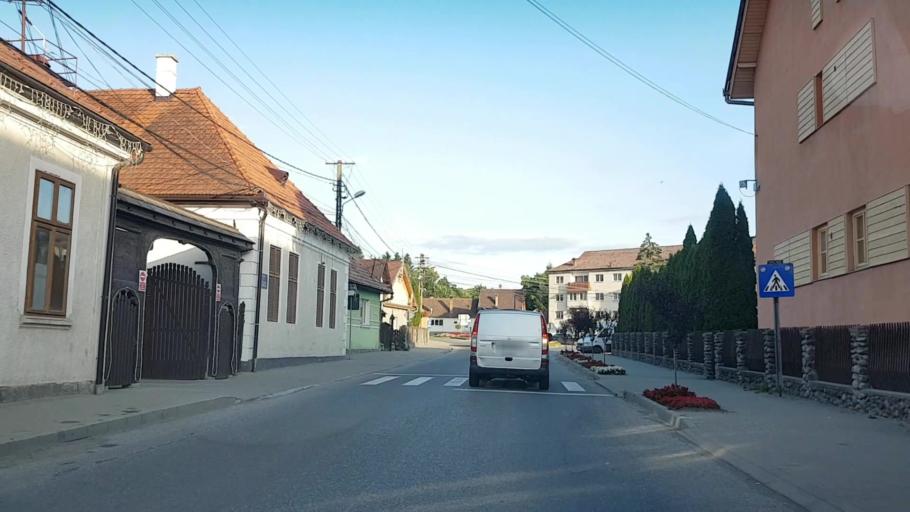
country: RO
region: Harghita
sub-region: Comuna Praid
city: Praid
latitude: 46.5517
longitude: 25.1271
